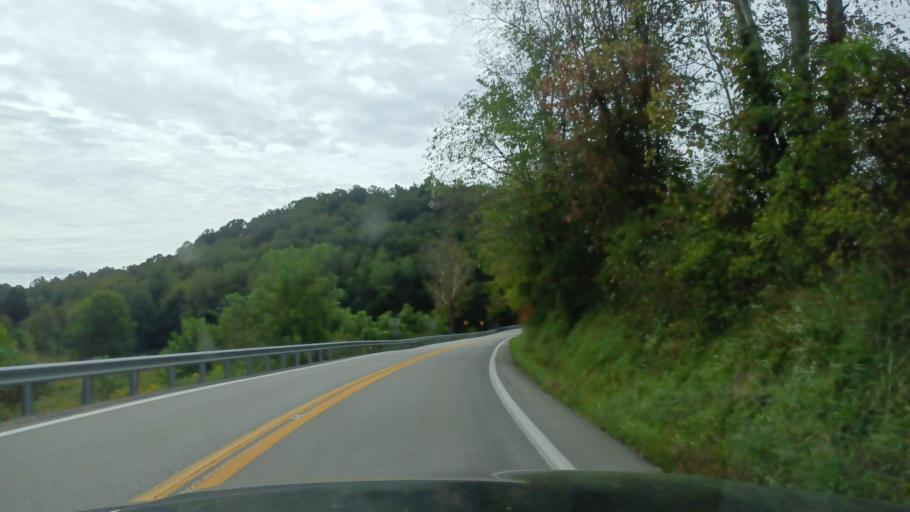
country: US
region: West Virginia
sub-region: Taylor County
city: Grafton
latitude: 39.3234
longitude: -80.1164
